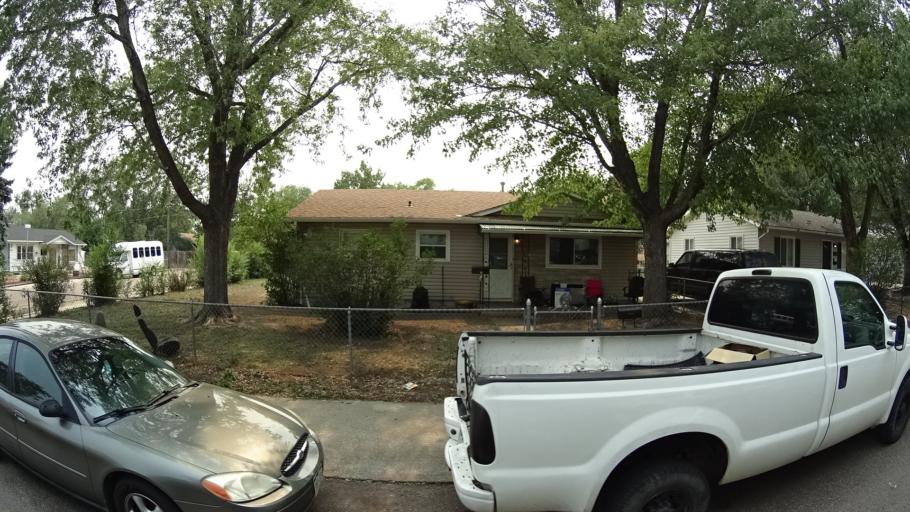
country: US
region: Colorado
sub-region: El Paso County
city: Stratmoor
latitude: 38.7975
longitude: -104.8069
